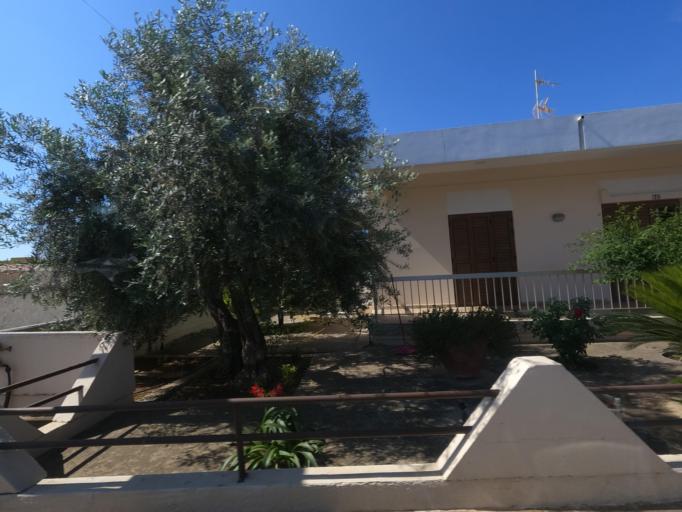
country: CY
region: Ammochostos
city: Frenaros
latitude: 35.0282
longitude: 33.9436
